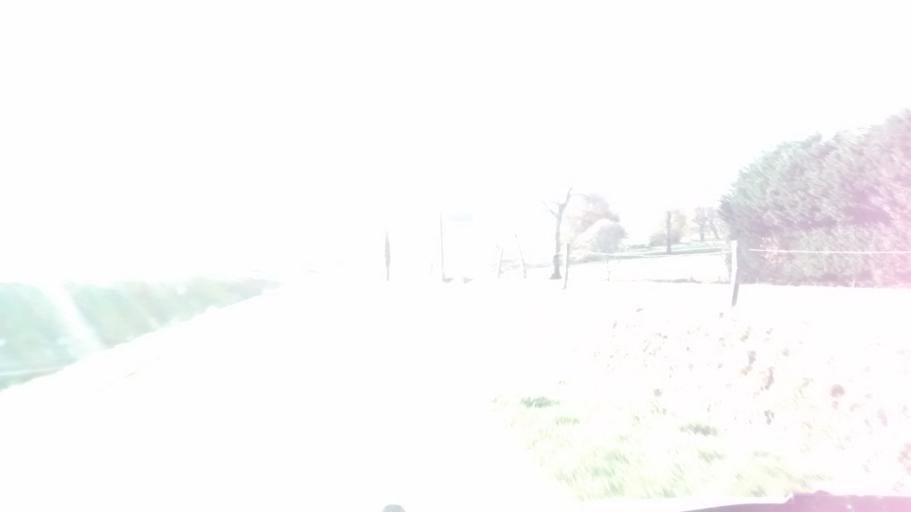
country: FR
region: Brittany
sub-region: Departement d'Ille-et-Vilaine
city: La Bouexiere
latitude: 48.2048
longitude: -1.4588
